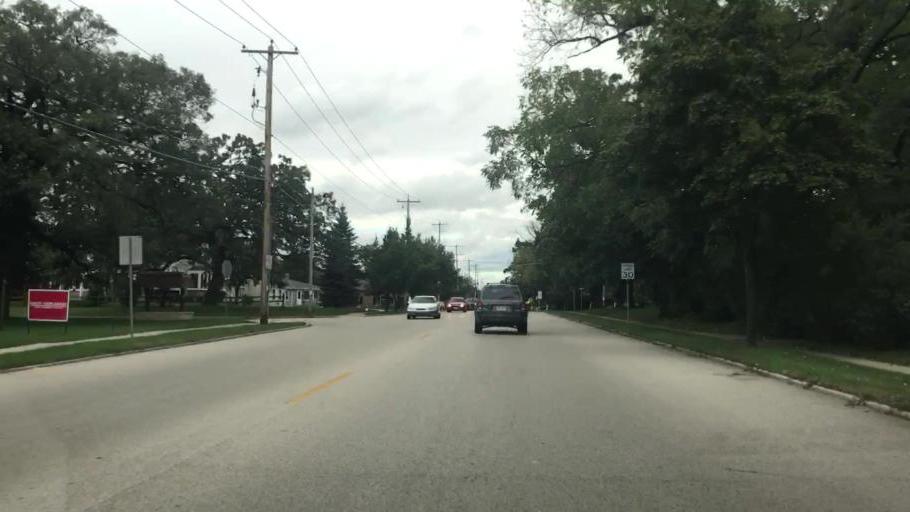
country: US
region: Wisconsin
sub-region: Waukesha County
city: Mukwonago
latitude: 42.8686
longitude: -88.3352
